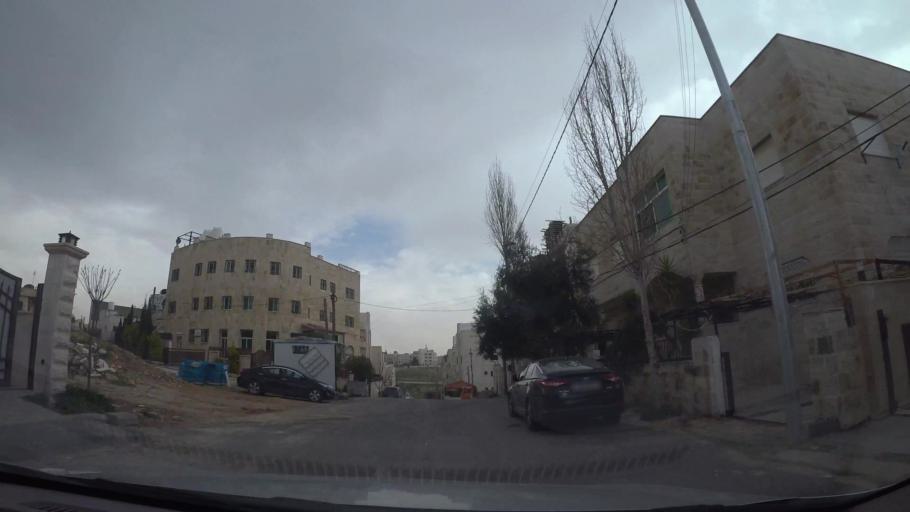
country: JO
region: Amman
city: Umm as Summaq
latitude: 31.9032
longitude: 35.8342
